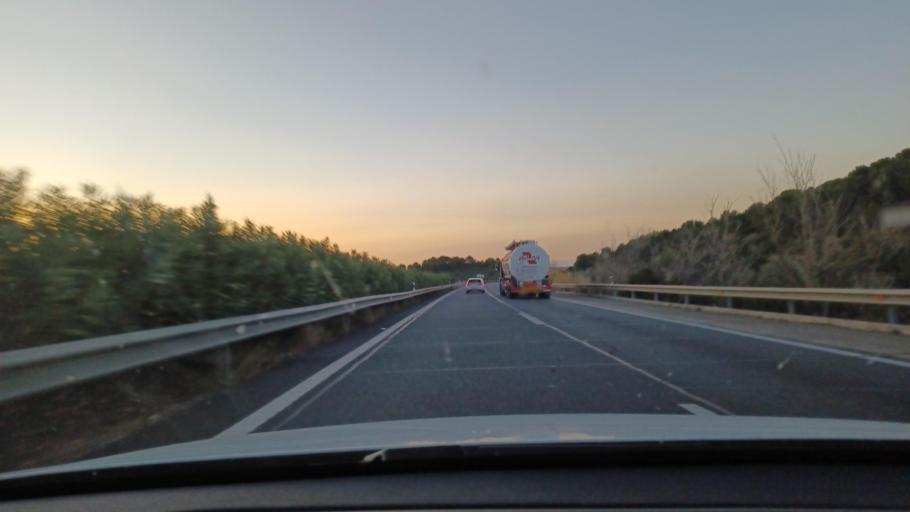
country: ES
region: Valencia
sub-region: Provincia de Castello
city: Alcala de Xivert
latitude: 40.2722
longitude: 0.2350
